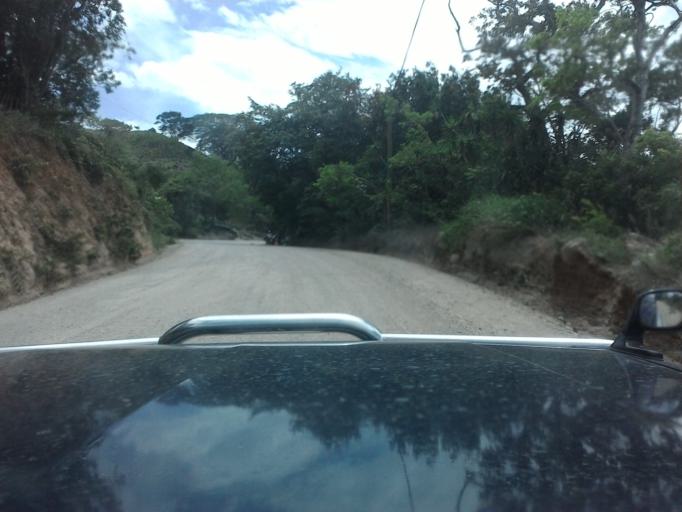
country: CR
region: Guanacaste
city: Juntas
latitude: 10.2358
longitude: -84.8534
